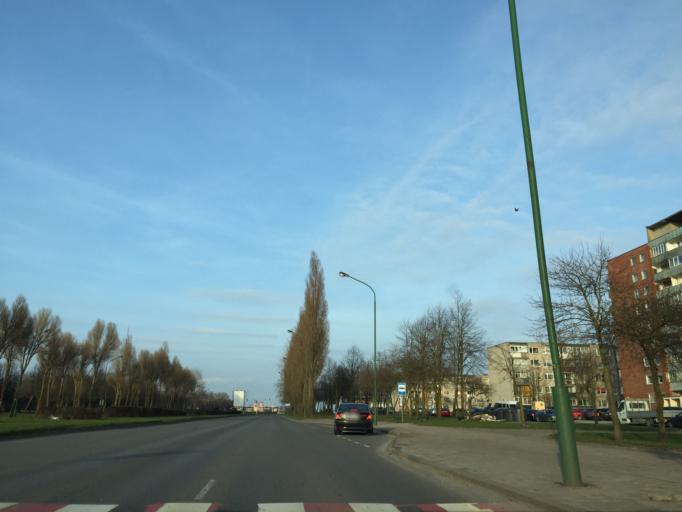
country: LT
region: Klaipedos apskritis
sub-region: Klaipeda
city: Klaipeda
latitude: 55.6906
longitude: 21.1729
